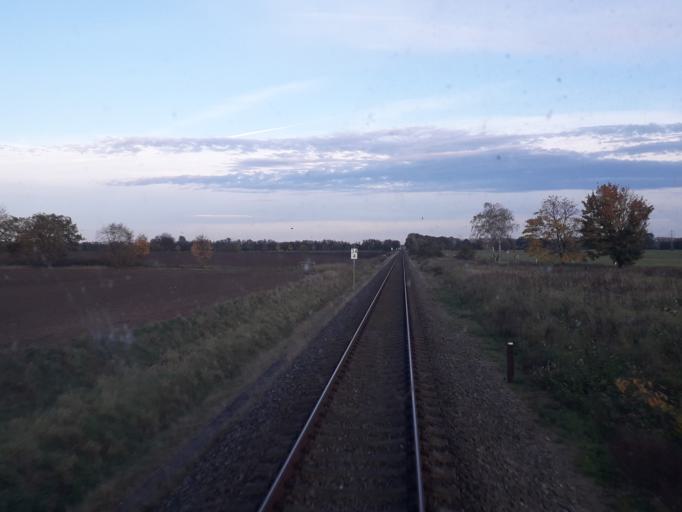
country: DE
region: Brandenburg
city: Dabergotz
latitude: 52.9346
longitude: 12.7215
